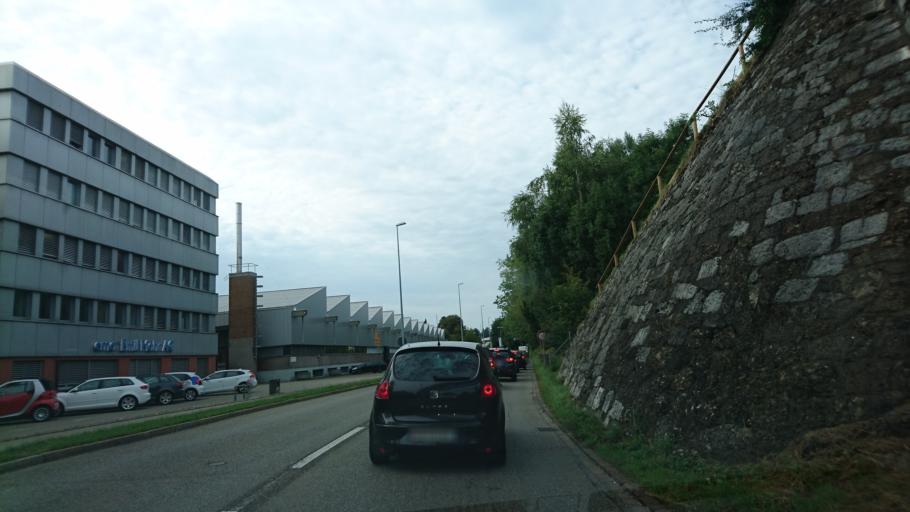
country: CH
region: Zurich
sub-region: Bezirk Hinwil
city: Wetzikon / Robenhausen
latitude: 47.3225
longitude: 8.7879
